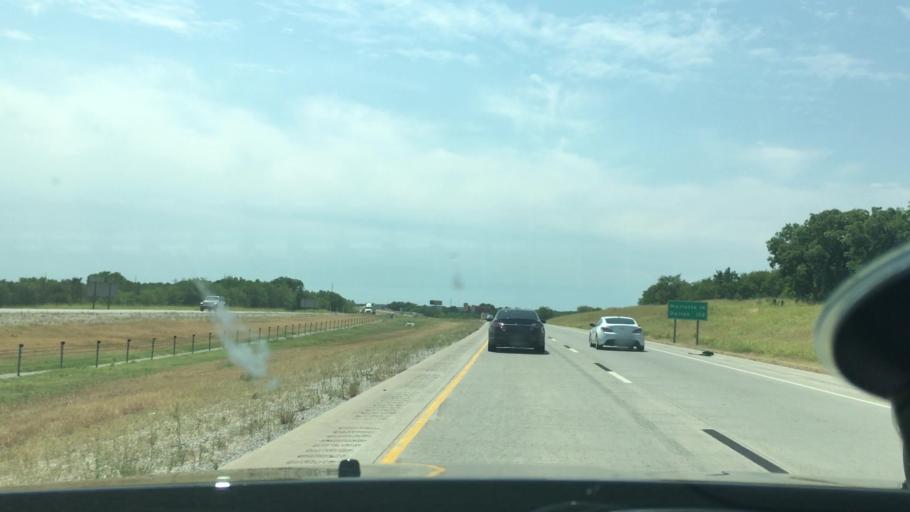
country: US
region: Oklahoma
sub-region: Carter County
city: Ardmore
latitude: 34.1271
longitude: -97.1567
